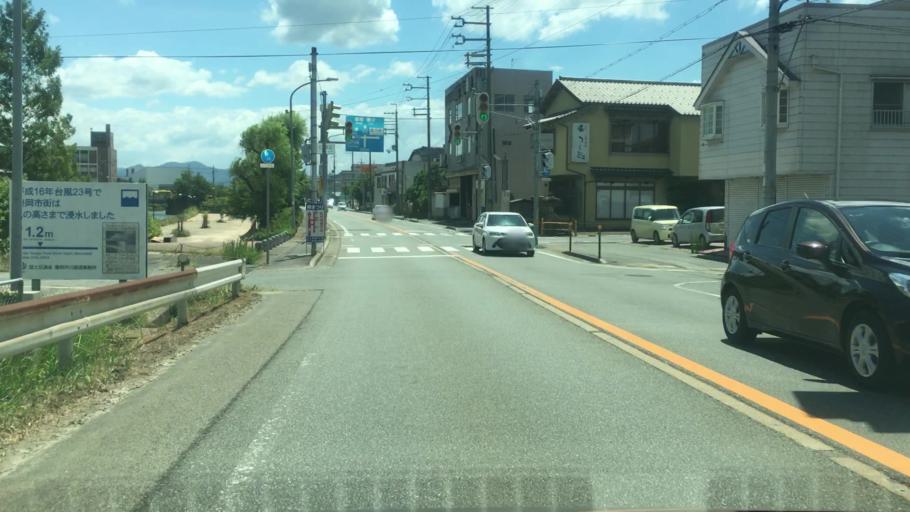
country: JP
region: Hyogo
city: Toyooka
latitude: 35.5464
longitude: 134.8258
